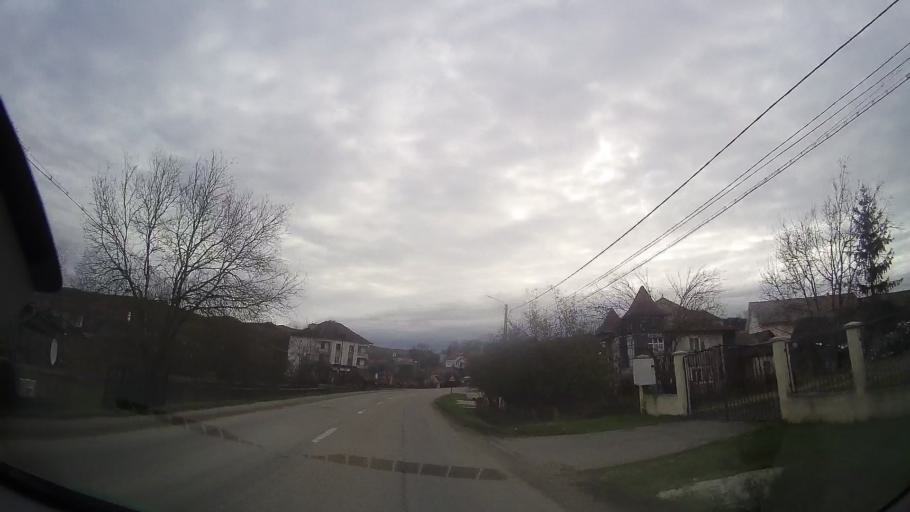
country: RO
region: Bistrita-Nasaud
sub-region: Comuna Budesti
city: Budesti
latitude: 46.8774
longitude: 24.2424
